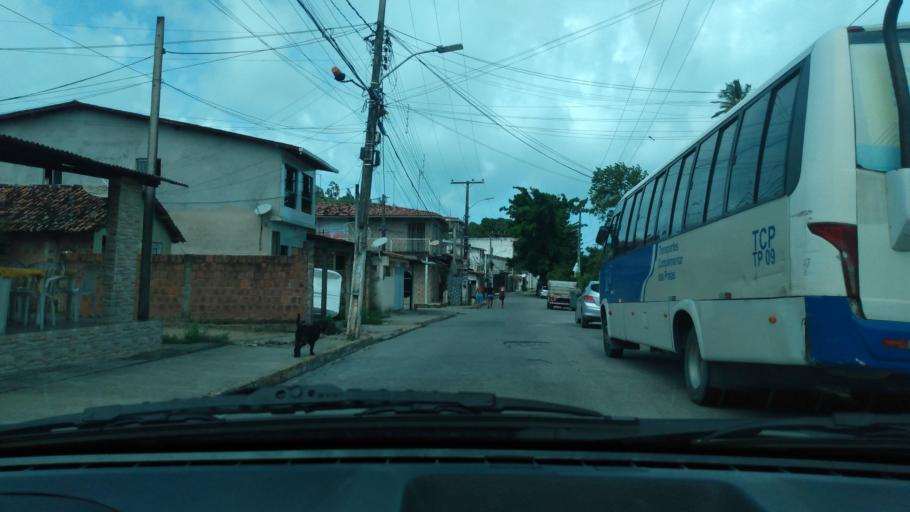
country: BR
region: Pernambuco
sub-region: Cabo De Santo Agostinho
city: Cabo
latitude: -8.3519
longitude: -34.9580
